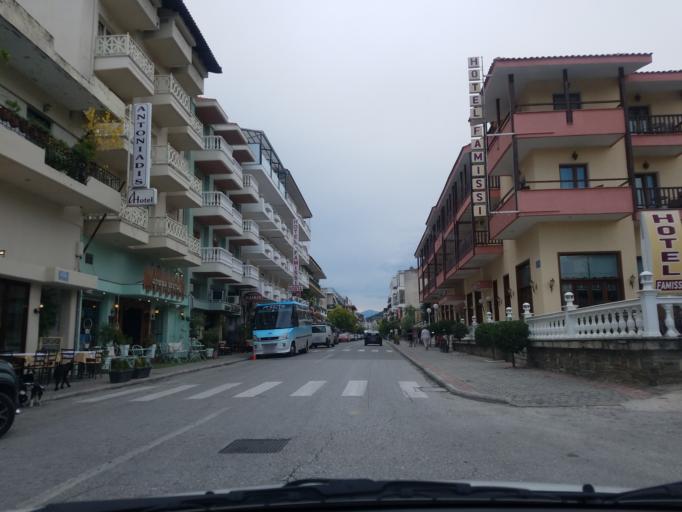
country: GR
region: Thessaly
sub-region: Trikala
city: Kalampaka
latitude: 39.7026
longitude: 21.6320
